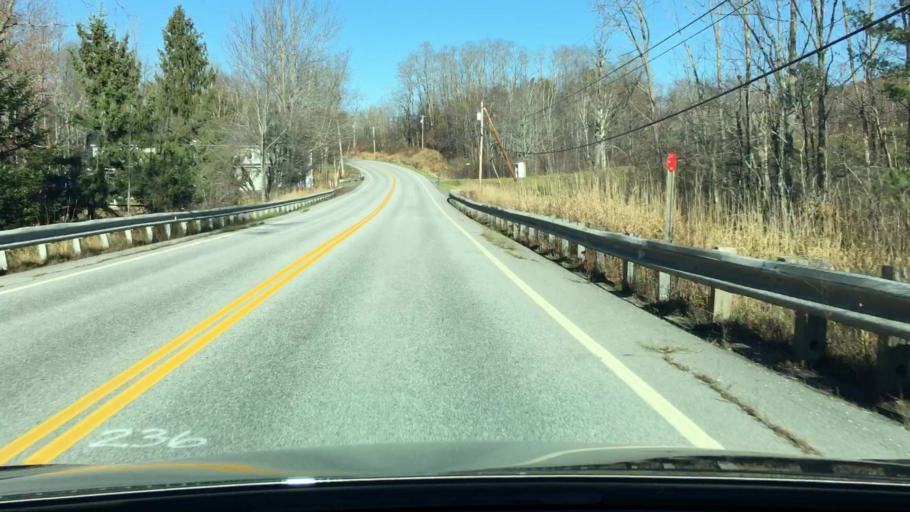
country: US
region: Maine
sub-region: Waldo County
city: Winterport
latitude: 44.6393
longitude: -68.8279
